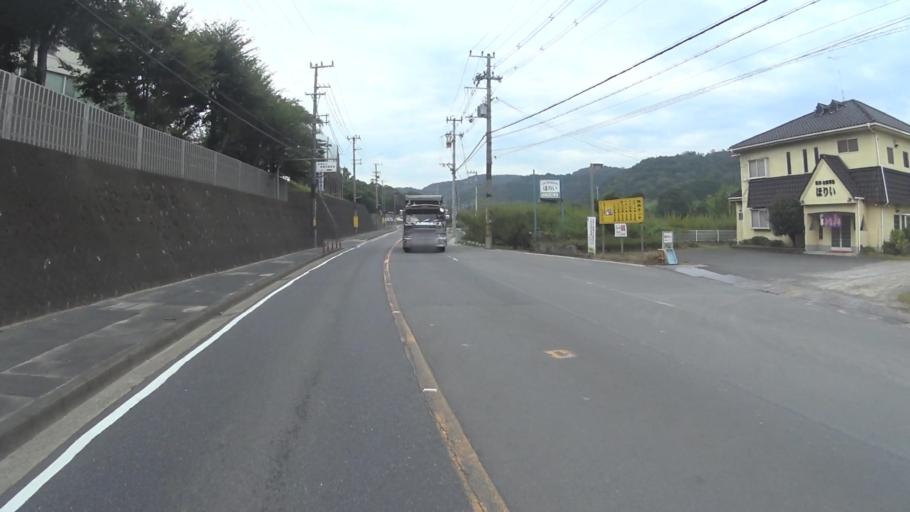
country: JP
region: Kyoto
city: Tanabe
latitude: 34.8309
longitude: 135.8154
